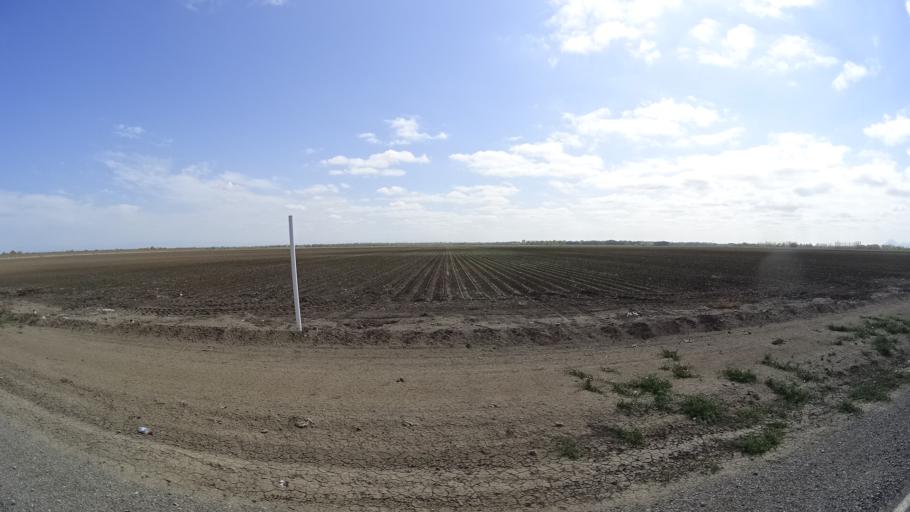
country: US
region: California
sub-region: Butte County
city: Biggs
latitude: 39.4383
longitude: -121.9299
